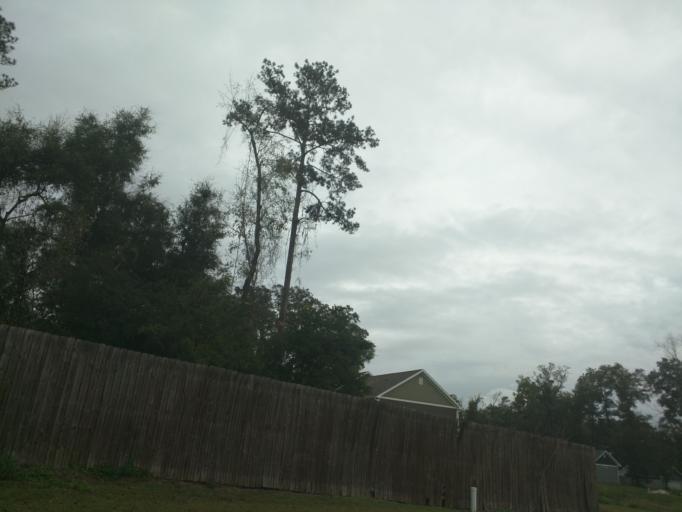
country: US
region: Florida
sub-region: Leon County
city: Tallahassee
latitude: 30.4632
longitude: -84.2325
